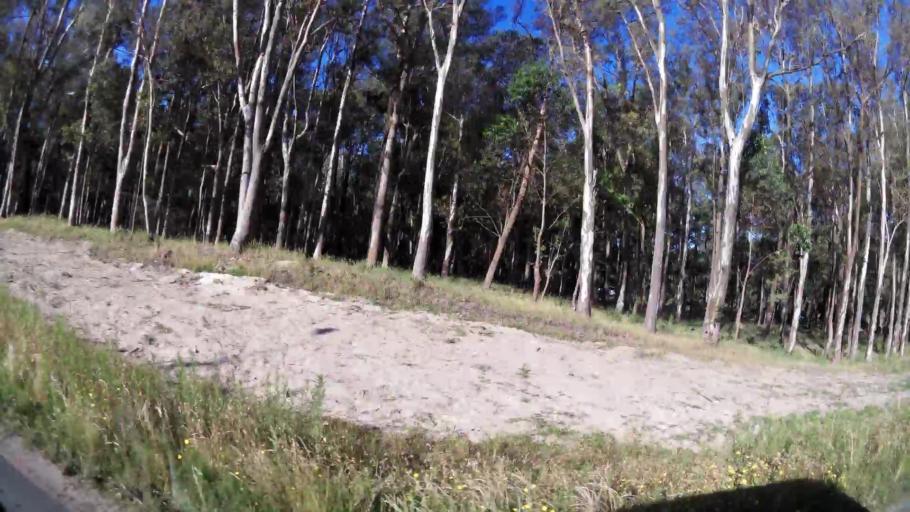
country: UY
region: Canelones
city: Barra de Carrasco
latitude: -34.8583
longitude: -56.0314
